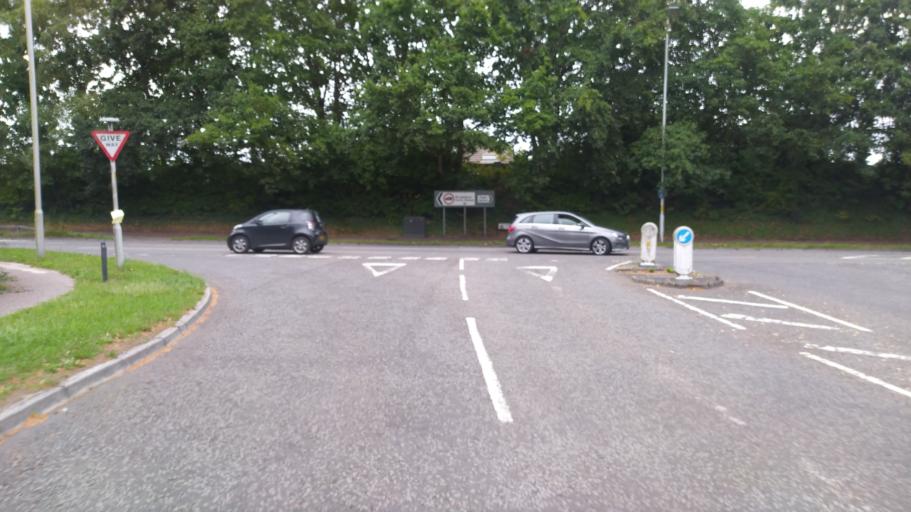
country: GB
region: England
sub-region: Dorset
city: Broadstone
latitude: 50.7518
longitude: -2.0031
